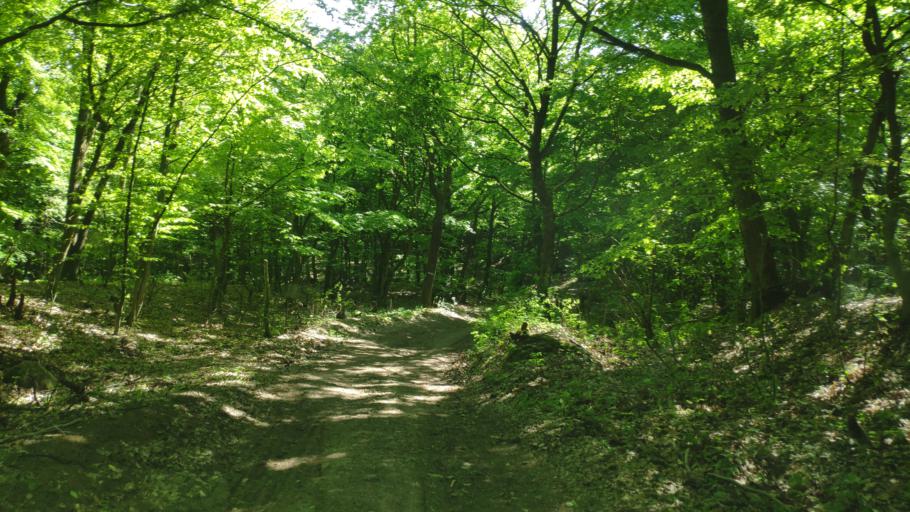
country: SK
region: Kosicky
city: Secovce
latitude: 48.7029
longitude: 21.5868
